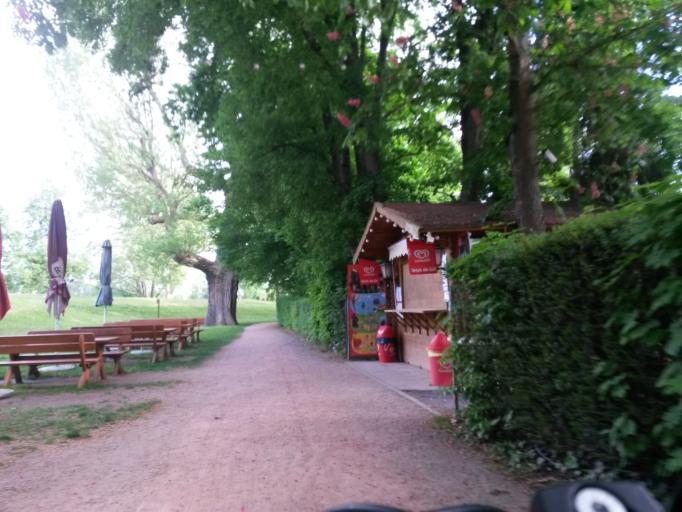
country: DE
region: Bavaria
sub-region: Regierungsbezirk Unterfranken
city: Bad Kissingen
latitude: 50.2016
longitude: 10.0731
